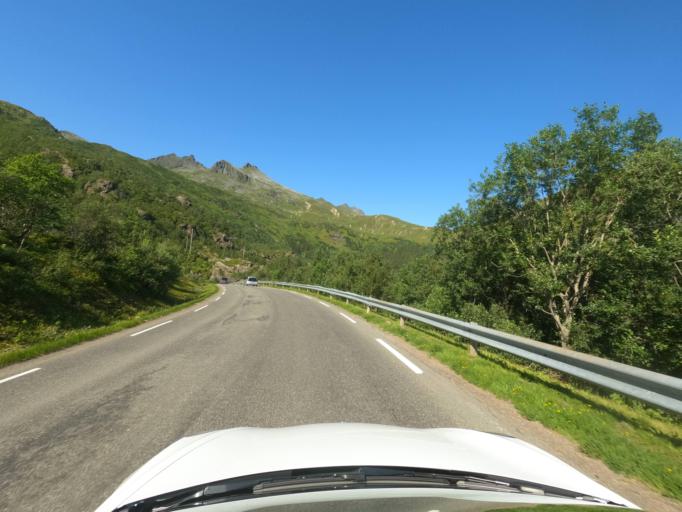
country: NO
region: Nordland
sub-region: Hadsel
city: Melbu
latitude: 68.3544
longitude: 14.7110
